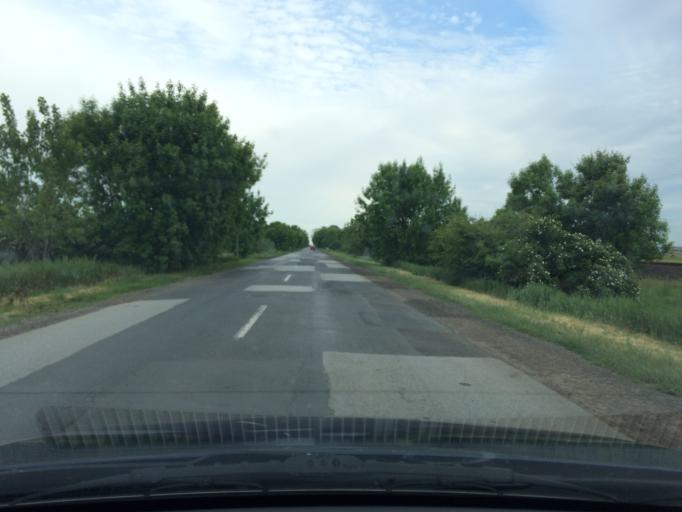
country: HU
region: Szabolcs-Szatmar-Bereg
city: Tiszavasvari
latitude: 47.9139
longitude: 21.3984
